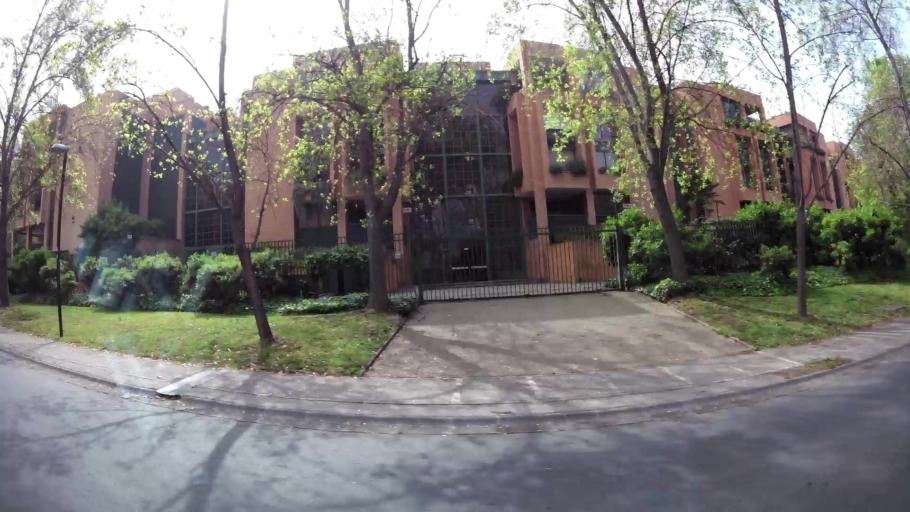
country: CL
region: Santiago Metropolitan
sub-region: Provincia de Santiago
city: Villa Presidente Frei, Nunoa, Santiago, Chile
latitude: -33.3730
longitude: -70.5711
